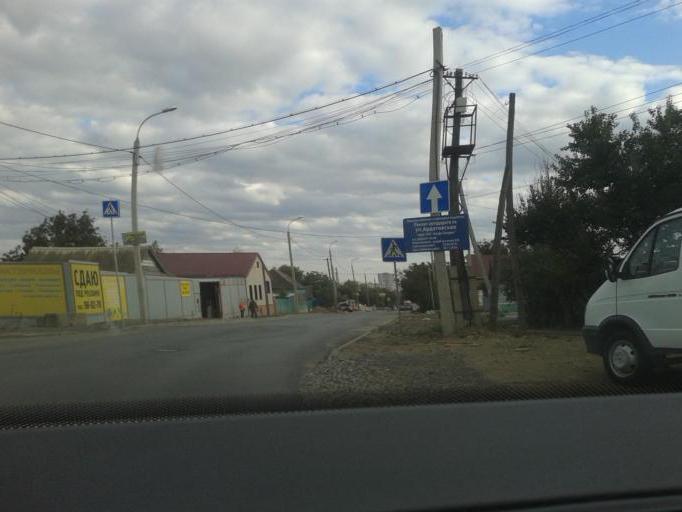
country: RU
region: Volgograd
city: Volgograd
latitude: 48.7021
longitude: 44.4608
